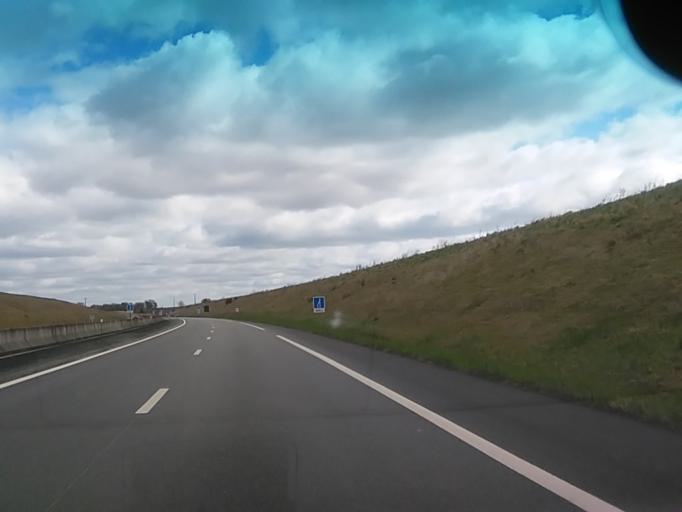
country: FR
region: Haute-Normandie
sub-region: Departement de l'Eure
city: Brionne
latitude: 49.1622
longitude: 0.6960
